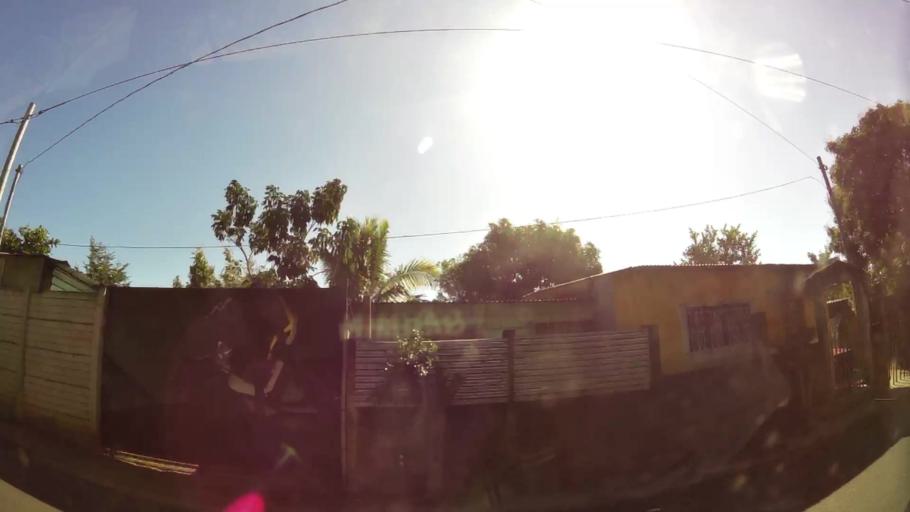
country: SV
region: Sonsonate
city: Sonzacate
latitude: 13.7331
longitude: -89.7193
